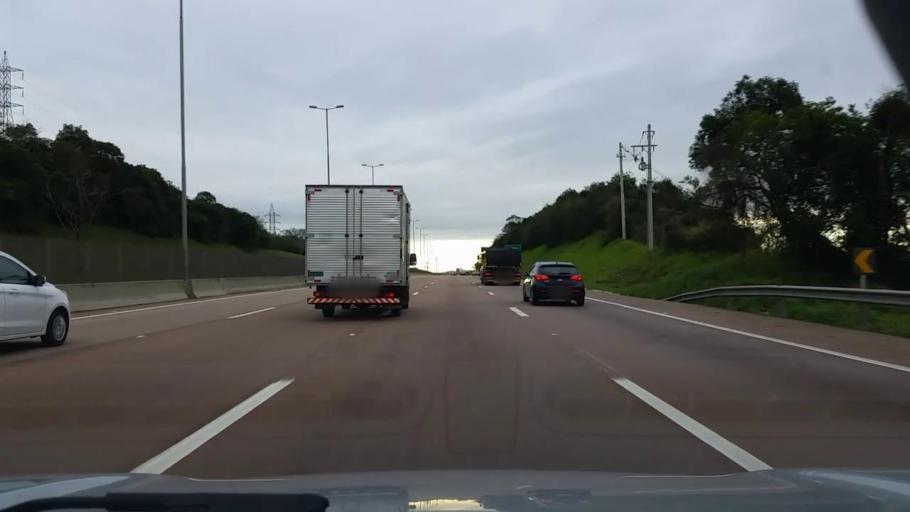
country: BR
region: Rio Grande do Sul
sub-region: Gravatai
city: Gravatai
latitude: -29.9560
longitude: -51.0098
